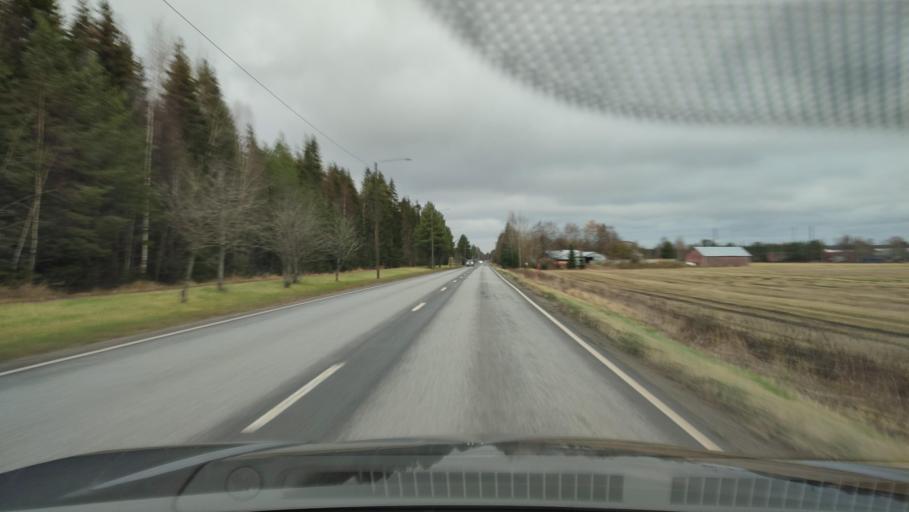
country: FI
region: Southern Ostrobothnia
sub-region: Suupohja
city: Kauhajoki
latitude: 62.4048
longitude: 22.1621
